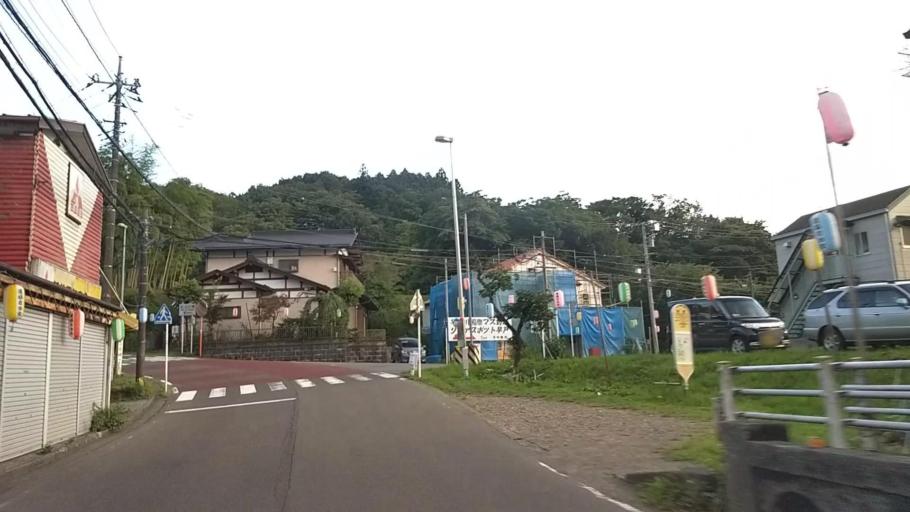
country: JP
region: Yamanashi
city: Uenohara
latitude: 35.5409
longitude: 139.2165
